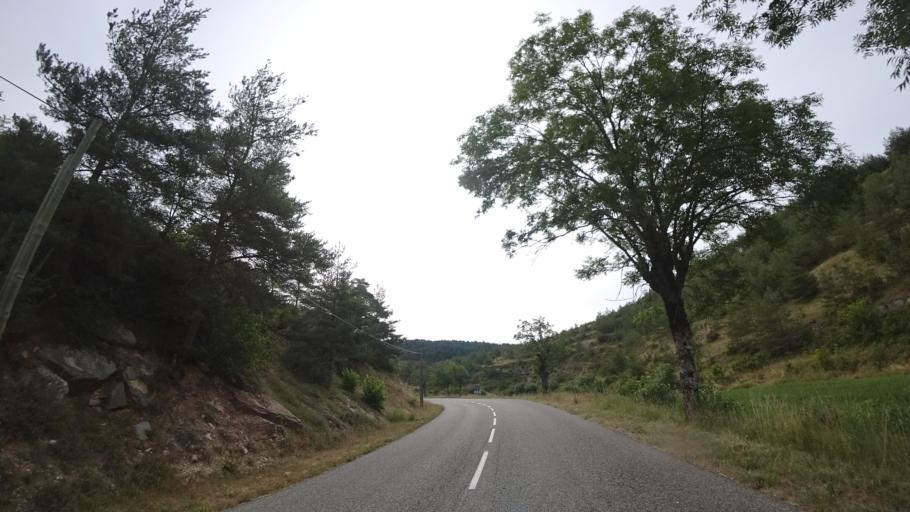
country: FR
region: Languedoc-Roussillon
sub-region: Departement de la Lozere
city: La Canourgue
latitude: 44.4069
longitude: 3.2831
